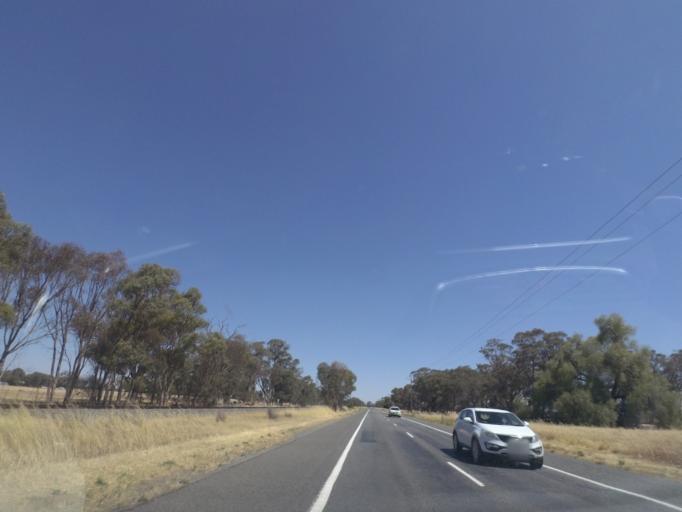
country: AU
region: Victoria
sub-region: Greater Shepparton
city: Shepparton
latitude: -36.2159
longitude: 145.4318
